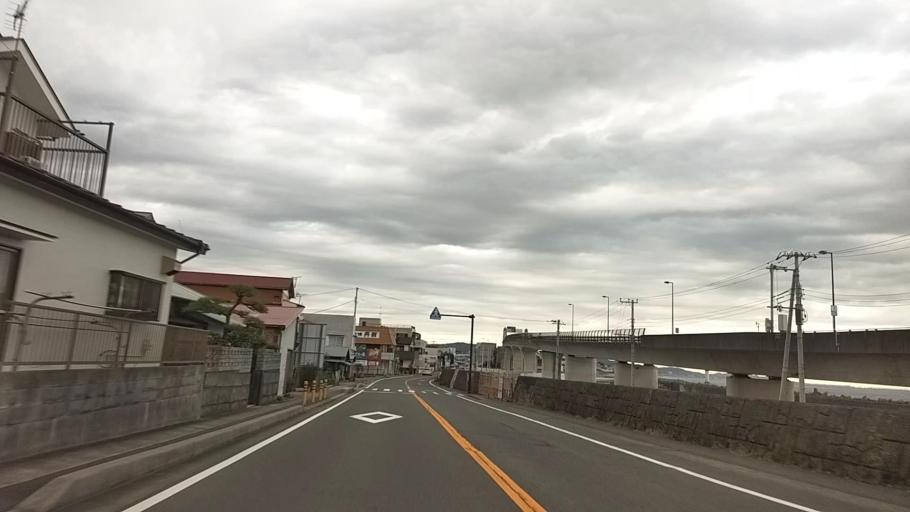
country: JP
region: Kanagawa
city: Odawara
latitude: 35.2359
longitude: 139.1450
